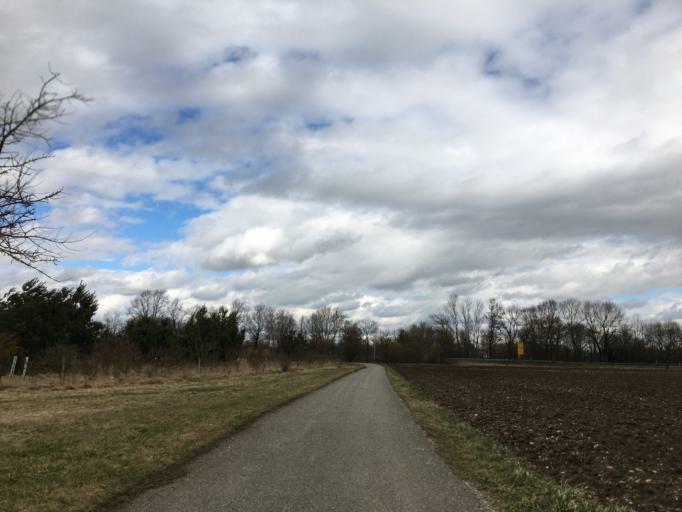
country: DE
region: Bavaria
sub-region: Upper Bavaria
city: Fuerstenfeldbruck
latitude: 48.1861
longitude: 11.2311
